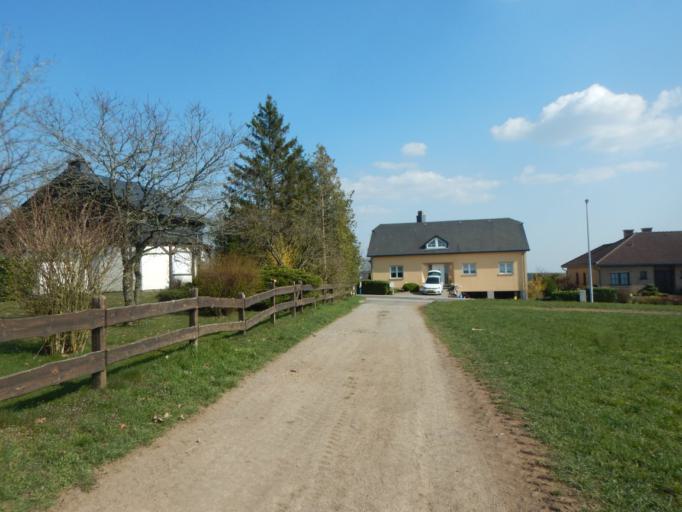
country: LU
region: Diekirch
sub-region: Canton de Diekirch
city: Bourscheid
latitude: 49.9514
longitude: 6.0804
